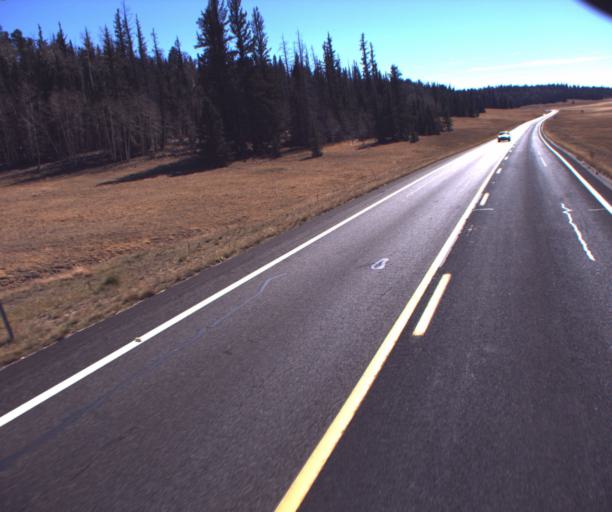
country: US
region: Arizona
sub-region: Coconino County
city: Grand Canyon
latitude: 36.4341
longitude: -112.1335
